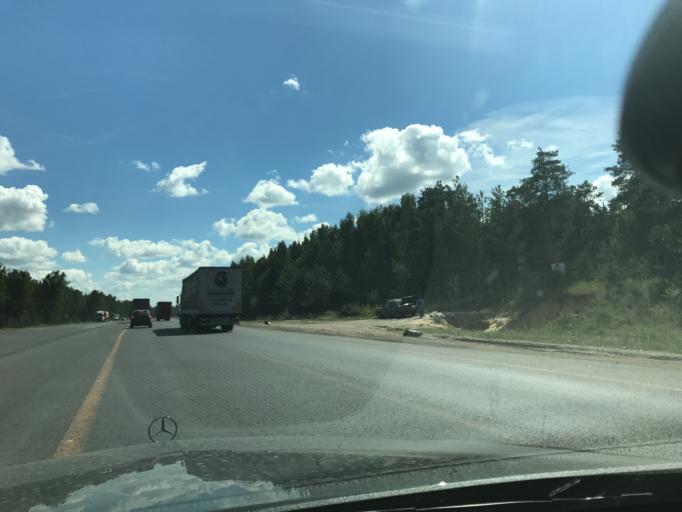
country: RU
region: Nizjnij Novgorod
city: Gorbatovka
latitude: 56.2959
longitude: 43.6933
